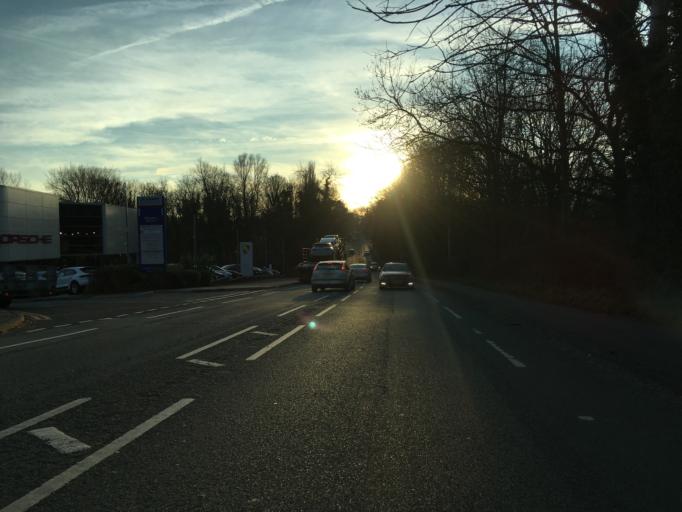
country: GB
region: England
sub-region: Cheshire East
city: Wilmslow
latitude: 53.3446
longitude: -2.2176
